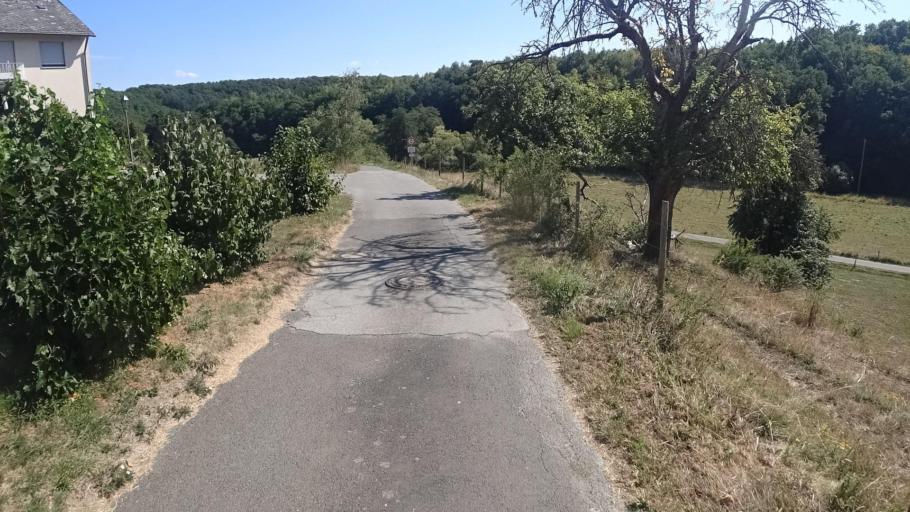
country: DE
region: Rheinland-Pfalz
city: Ravengiersburg
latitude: 49.9343
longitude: 7.4785
